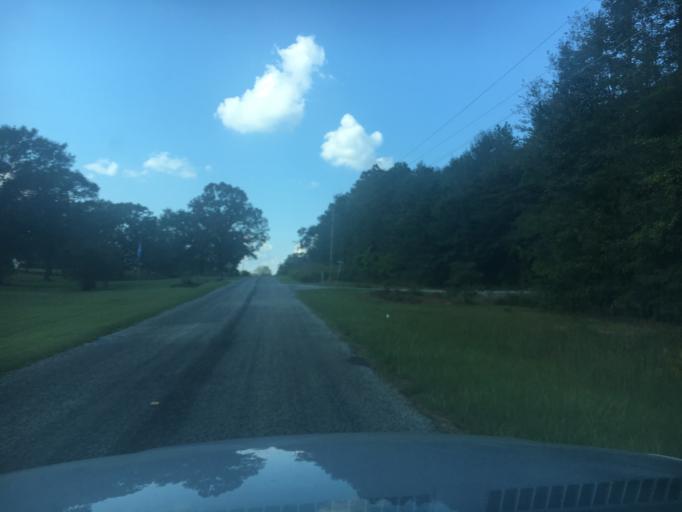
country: US
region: South Carolina
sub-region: Greenwood County
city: Ware Shoals
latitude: 34.5012
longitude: -82.2324
